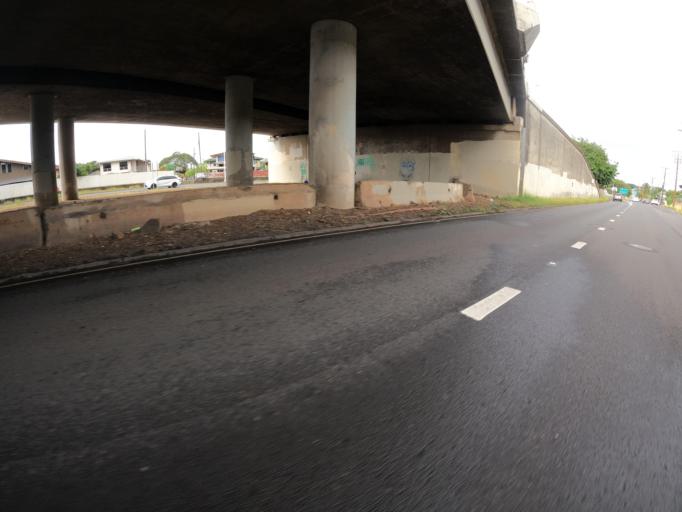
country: US
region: Hawaii
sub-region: Honolulu County
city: Honolulu
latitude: 21.3246
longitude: -157.8656
